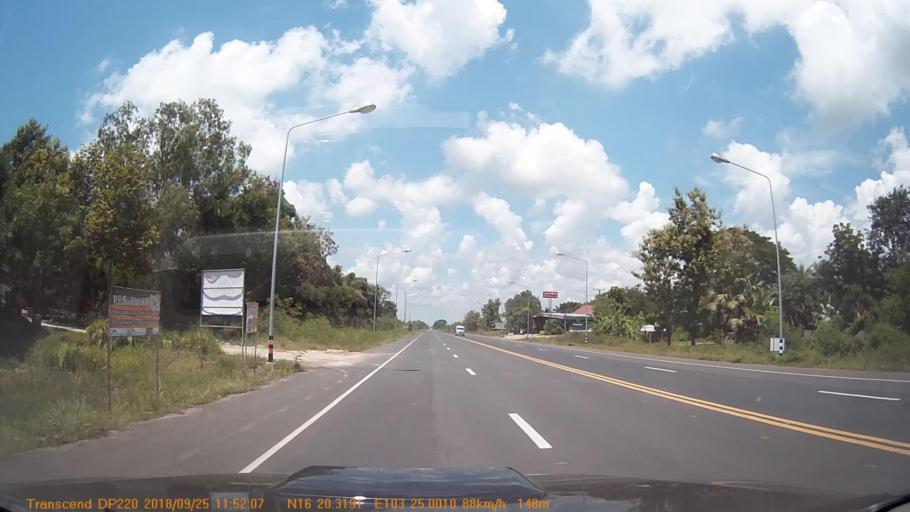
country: TH
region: Kalasin
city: Yang Talat
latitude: 16.3387
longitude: 103.4167
